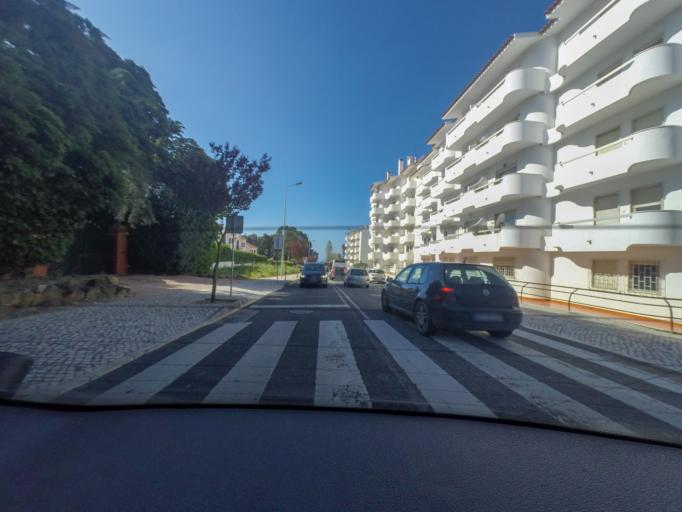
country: PT
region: Lisbon
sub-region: Cascais
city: Monte Estoril
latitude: 38.7142
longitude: -9.4177
